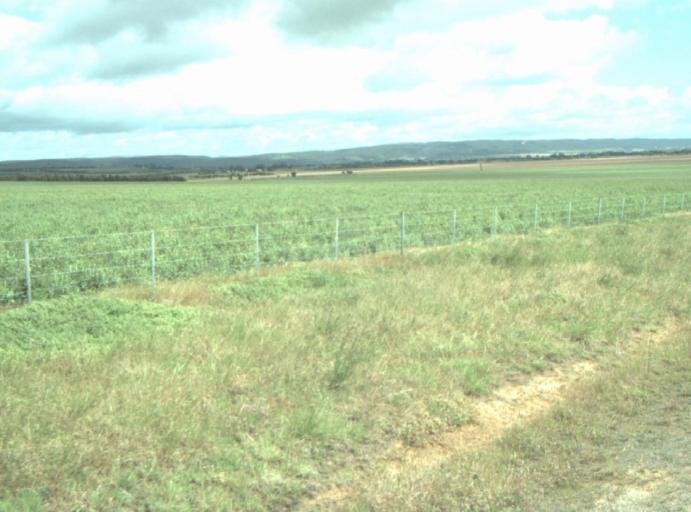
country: AU
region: Victoria
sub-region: Greater Geelong
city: Lara
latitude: -37.8885
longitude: 144.3502
